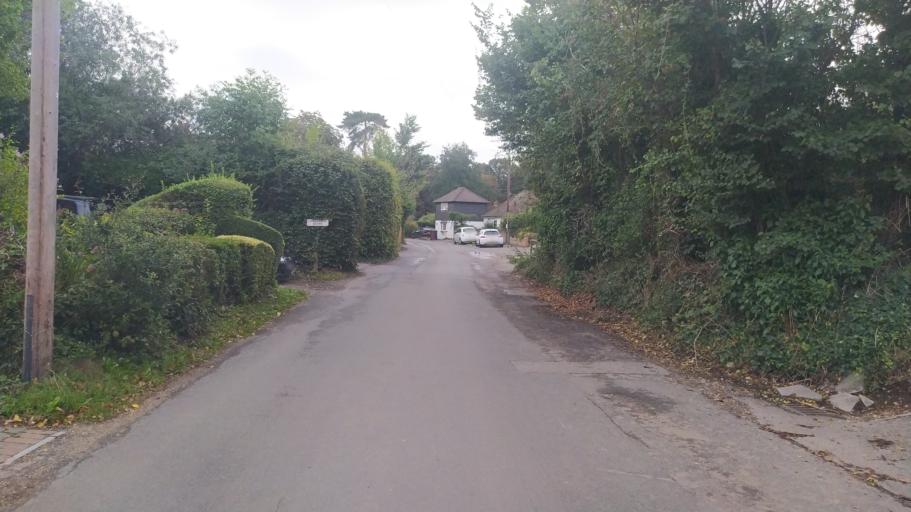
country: GB
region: England
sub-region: West Sussex
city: Chichester
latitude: 50.8140
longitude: -0.7513
